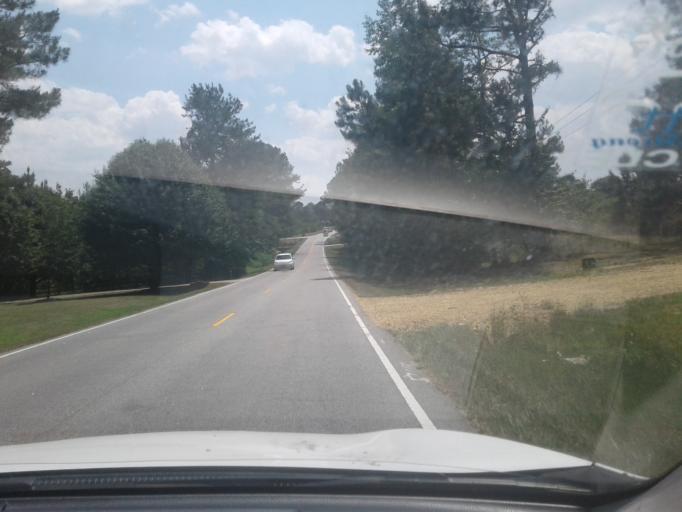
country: US
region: North Carolina
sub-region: Johnston County
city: Benson
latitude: 35.4082
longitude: -78.5405
